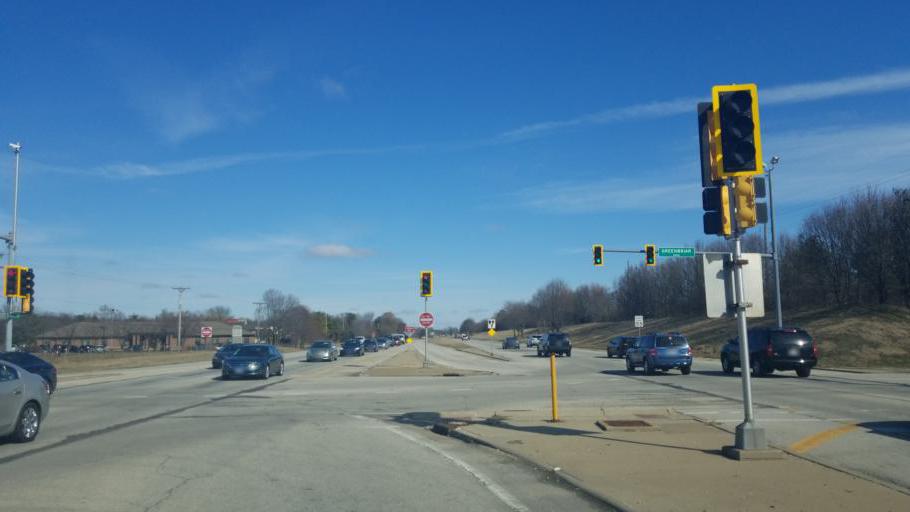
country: US
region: Illinois
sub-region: Sangamon County
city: Jerome
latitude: 39.7752
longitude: -89.7066
